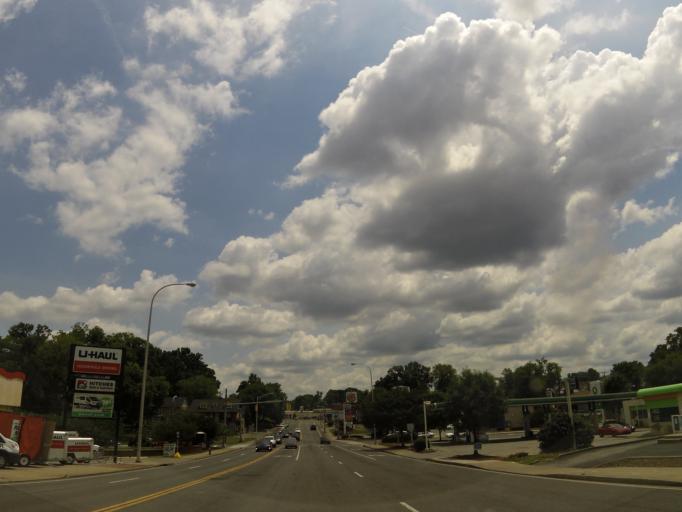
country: US
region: Tennessee
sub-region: Davidson County
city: Nashville
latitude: 36.1352
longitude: -86.7790
